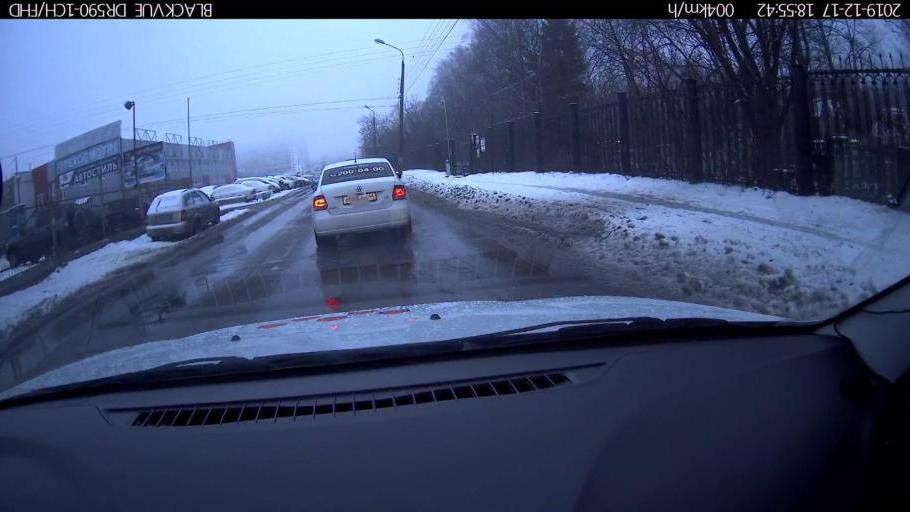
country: RU
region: Nizjnij Novgorod
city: Nizhniy Novgorod
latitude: 56.2841
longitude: 43.9985
